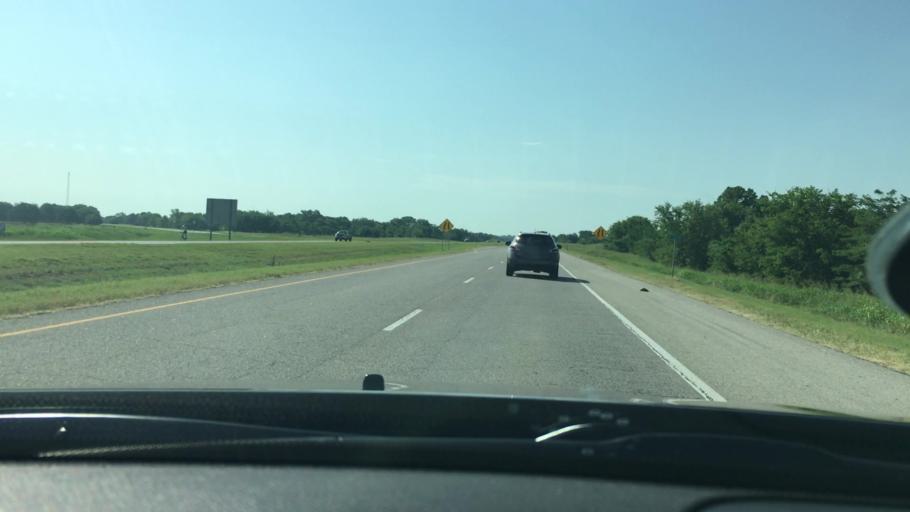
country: US
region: Oklahoma
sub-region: Pontotoc County
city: Ada
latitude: 34.7227
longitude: -96.6312
